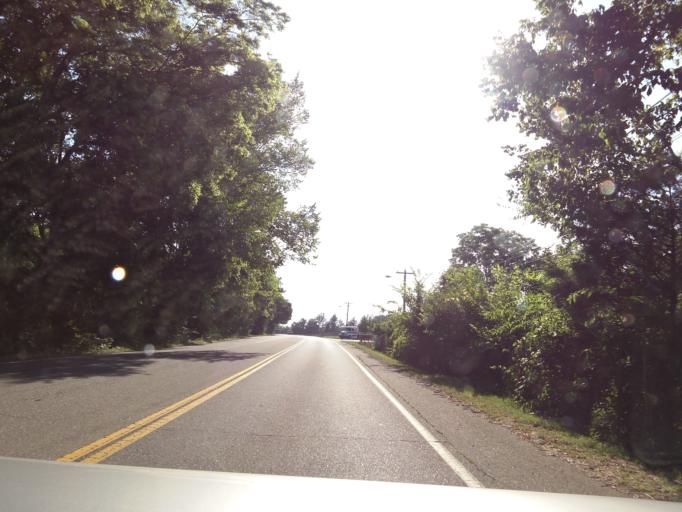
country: US
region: Tennessee
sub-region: Blount County
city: Alcoa
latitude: 35.8065
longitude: -83.9700
